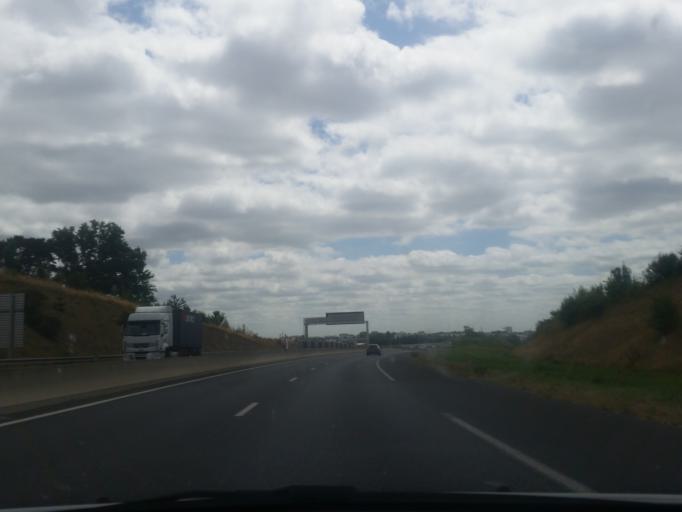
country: FR
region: Pays de la Loire
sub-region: Departement de Maine-et-Loire
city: Angers
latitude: 47.4960
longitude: -0.5505
